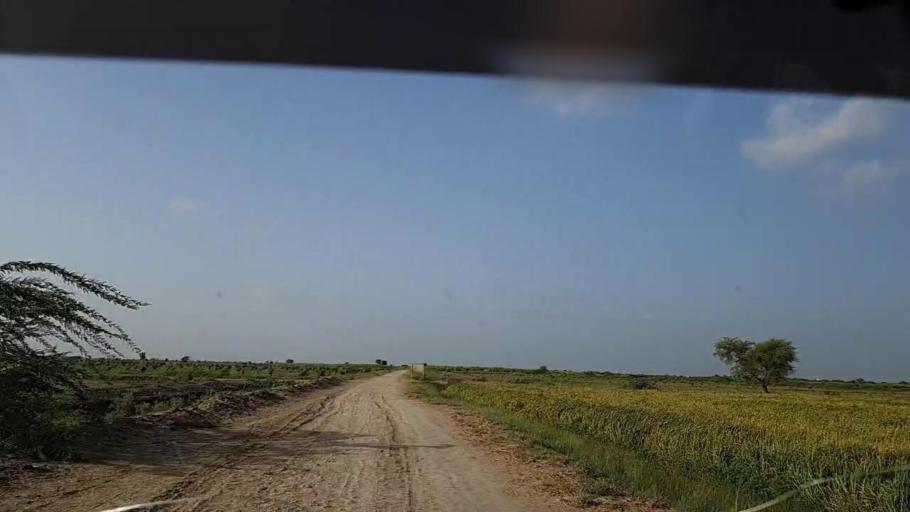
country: PK
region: Sindh
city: Badin
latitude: 24.5633
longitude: 68.8826
